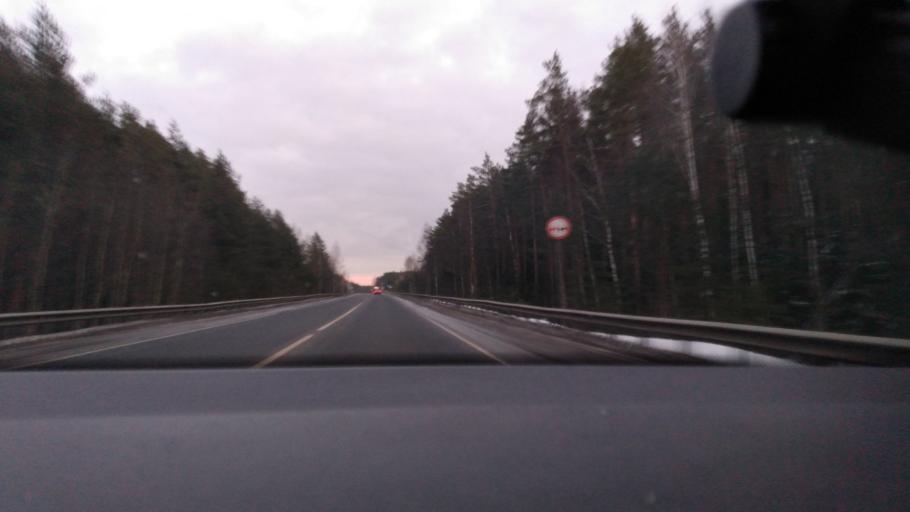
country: RU
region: Moskovskaya
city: Il'inskiy Pogost
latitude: 55.4800
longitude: 38.9373
